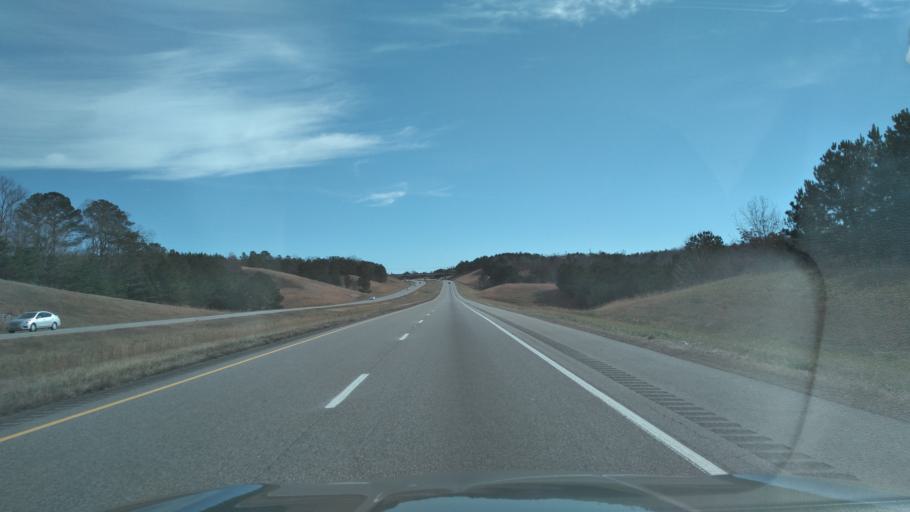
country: US
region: Alabama
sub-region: Marion County
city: Guin
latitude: 34.0542
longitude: -87.9414
